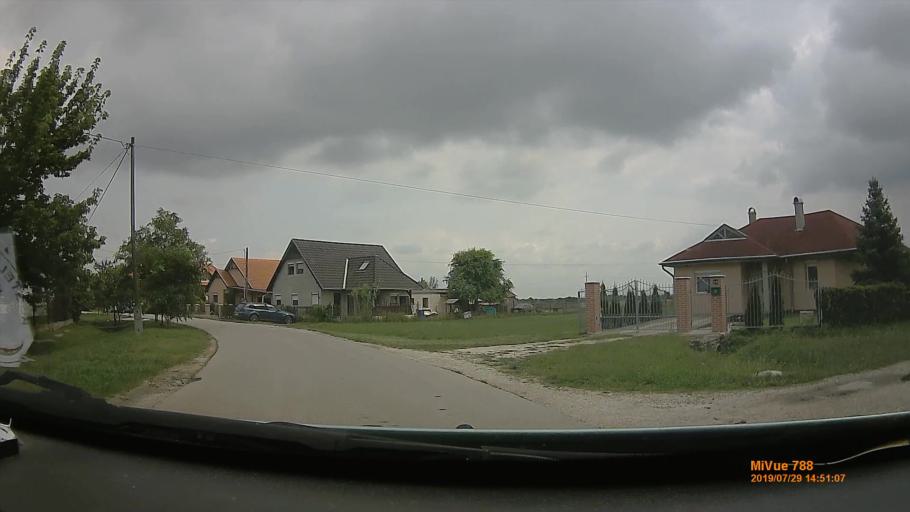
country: HU
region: Fejer
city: Lepseny
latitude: 47.0150
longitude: 18.2076
